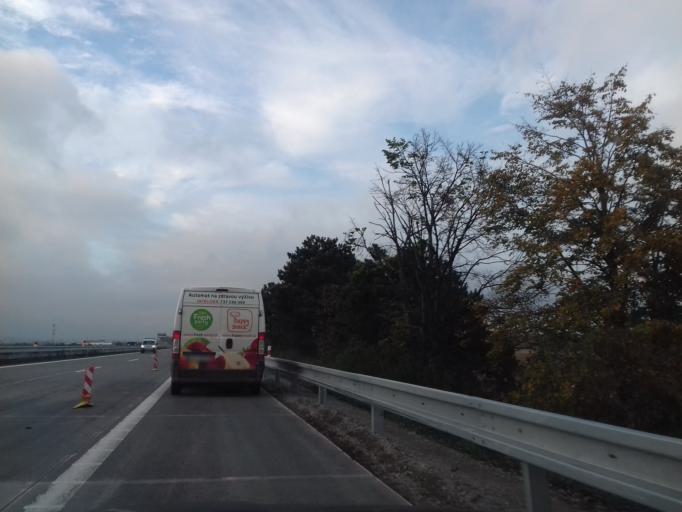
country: CZ
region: South Moravian
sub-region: Okres Brno-Venkov
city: Blucina
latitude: 49.0473
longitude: 16.6762
